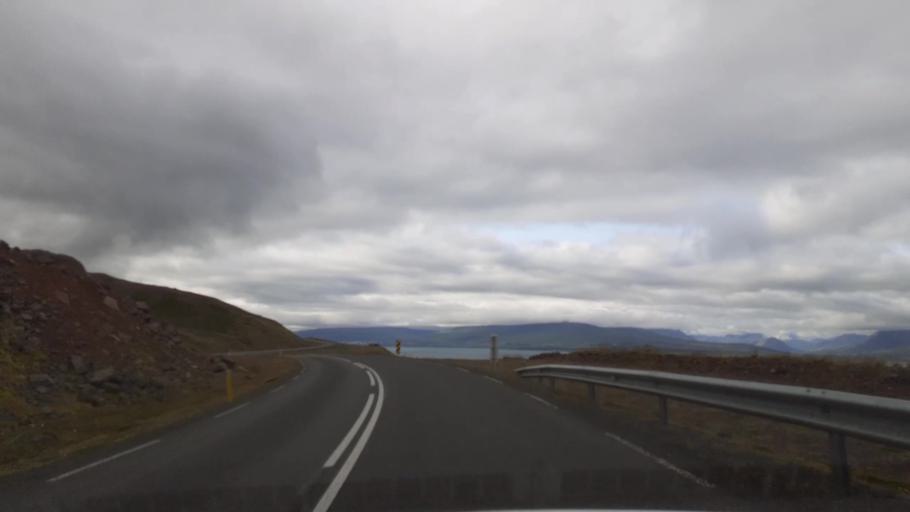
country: IS
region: Northeast
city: Akureyri
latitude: 65.8353
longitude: -18.0554
